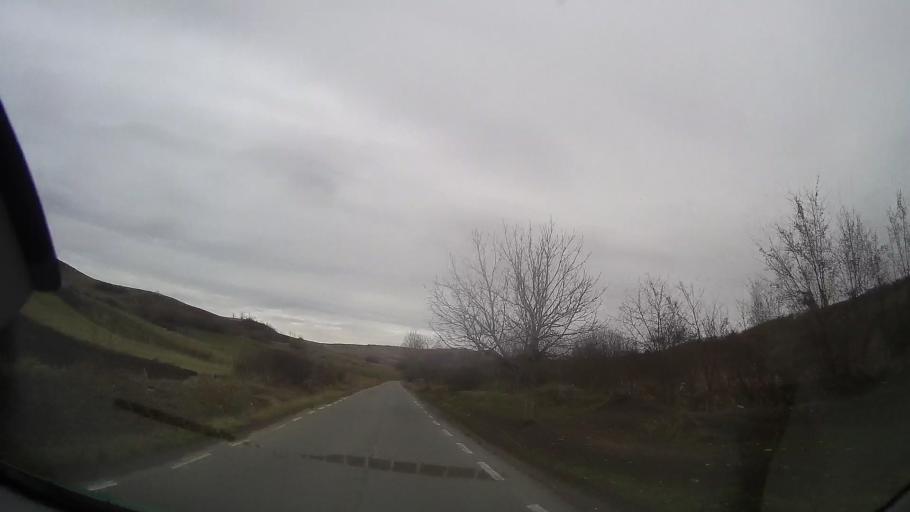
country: RO
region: Mures
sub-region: Comuna Bala
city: Bala
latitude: 46.7143
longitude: 24.5309
